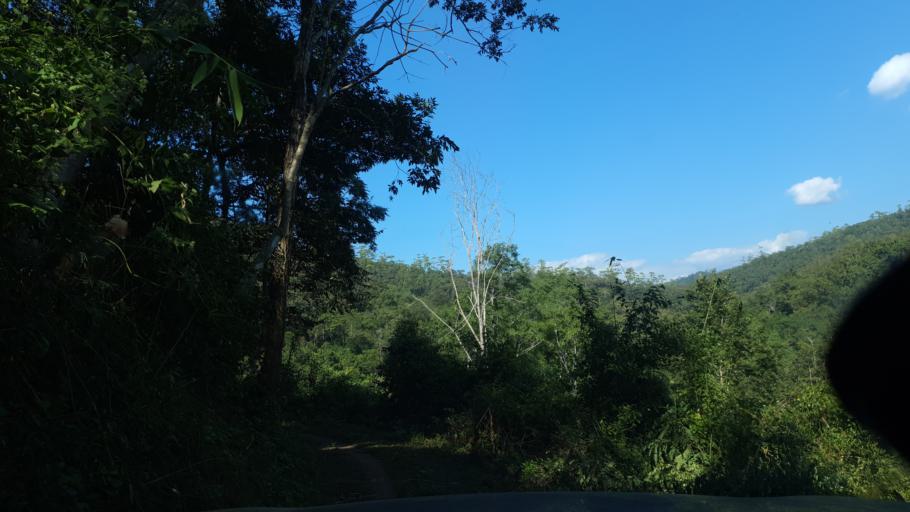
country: TH
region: Mae Hong Son
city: Mae Hi
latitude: 19.3050
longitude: 98.6997
